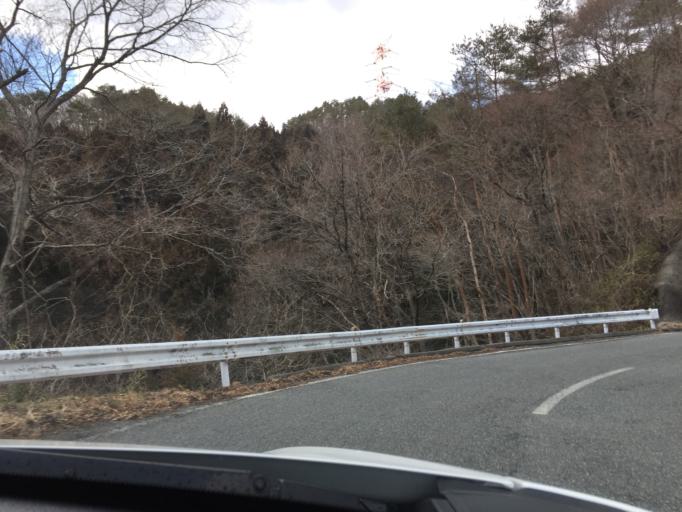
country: JP
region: Fukushima
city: Iwaki
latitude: 37.2096
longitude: 140.7439
